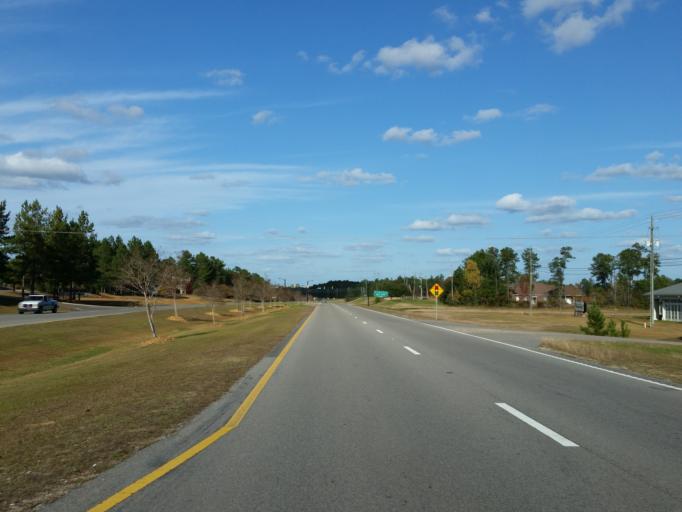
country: US
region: Mississippi
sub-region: Forrest County
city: Hattiesburg
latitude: 31.2790
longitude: -89.3265
